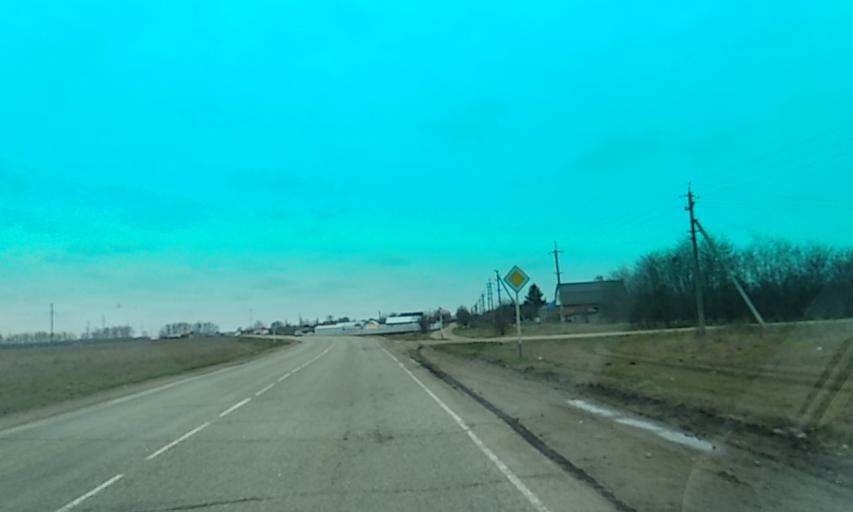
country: RU
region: Krasnodarskiy
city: Ust'-Labinsk
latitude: 45.3704
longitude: 39.7091
